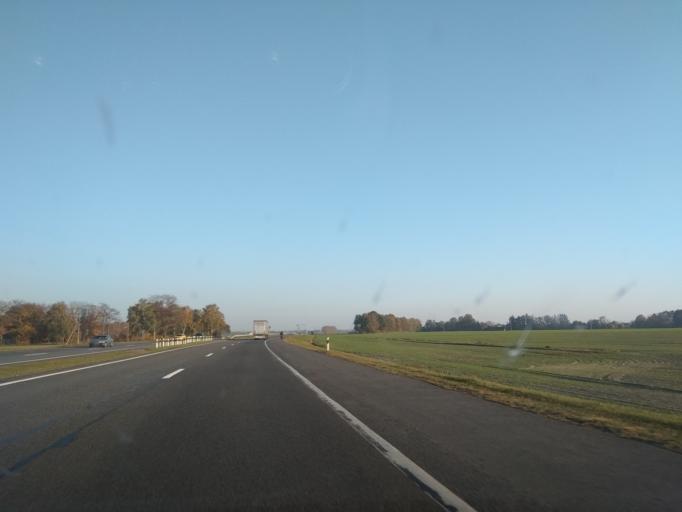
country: BY
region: Brest
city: Kobryn
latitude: 52.1970
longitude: 24.2995
